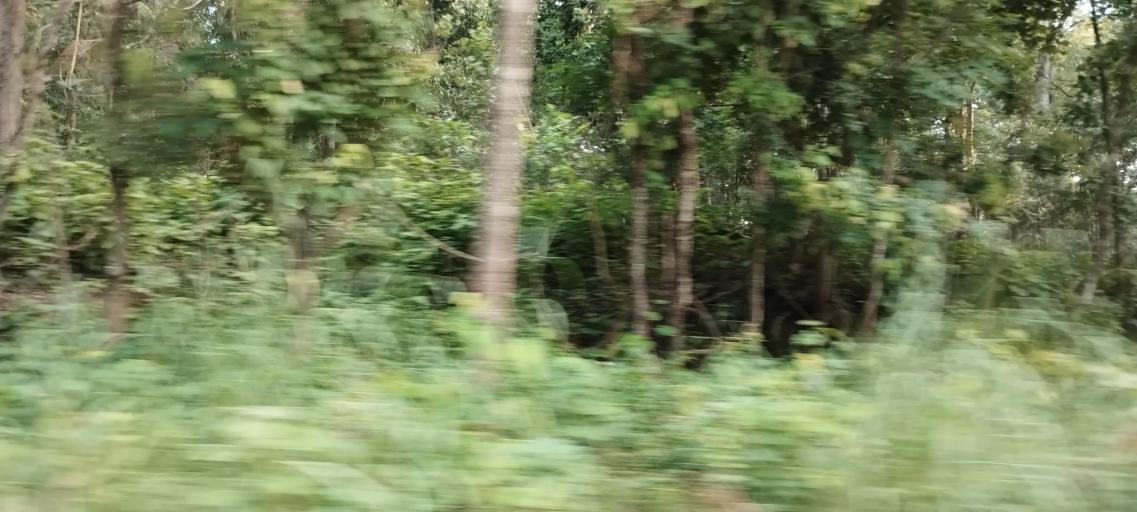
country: NP
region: Mid Western
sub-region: Bheri Zone
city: Bardiya
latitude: 28.4288
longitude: 81.3742
